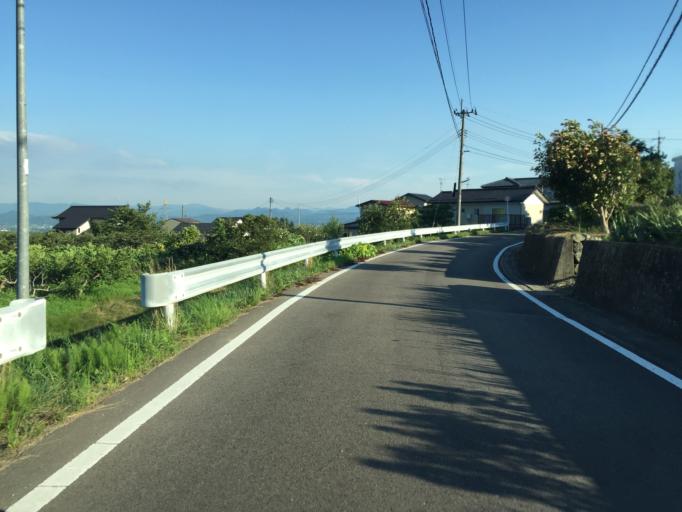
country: JP
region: Fukushima
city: Hobaramachi
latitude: 37.8778
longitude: 140.5191
